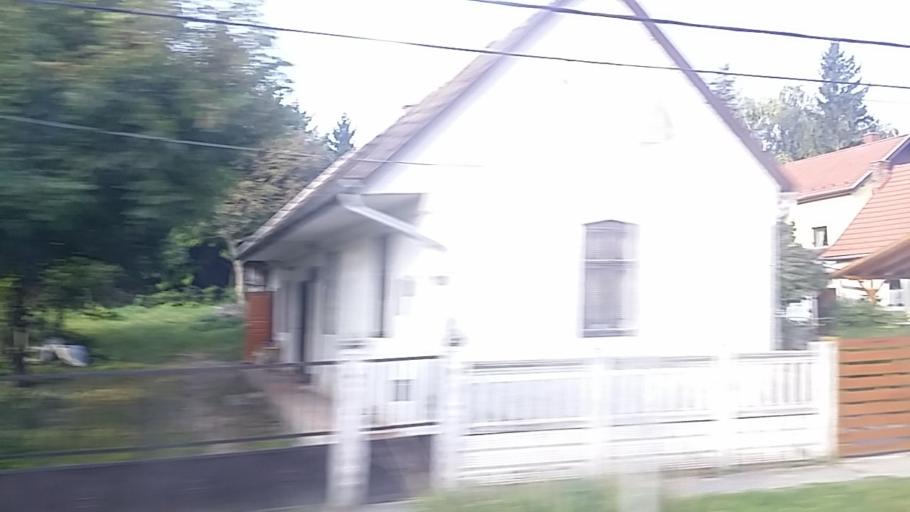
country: HU
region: Pest
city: Pilisvorosvar
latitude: 47.6208
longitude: 18.9027
